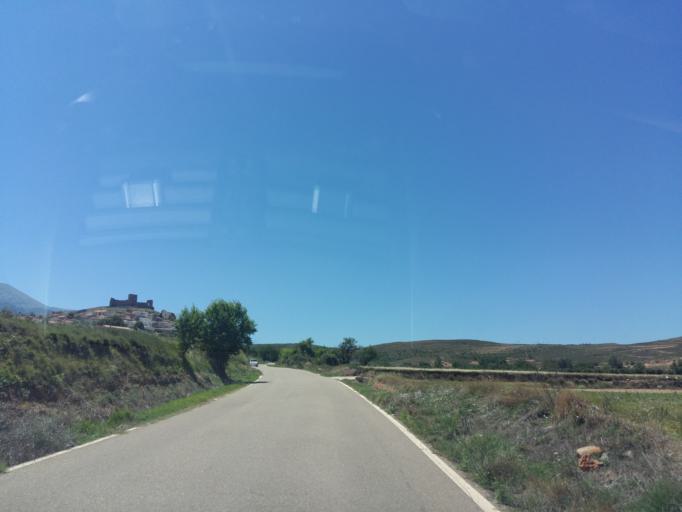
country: ES
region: Aragon
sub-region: Provincia de Zaragoza
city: Trasmoz
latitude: 41.8281
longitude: -1.7155
